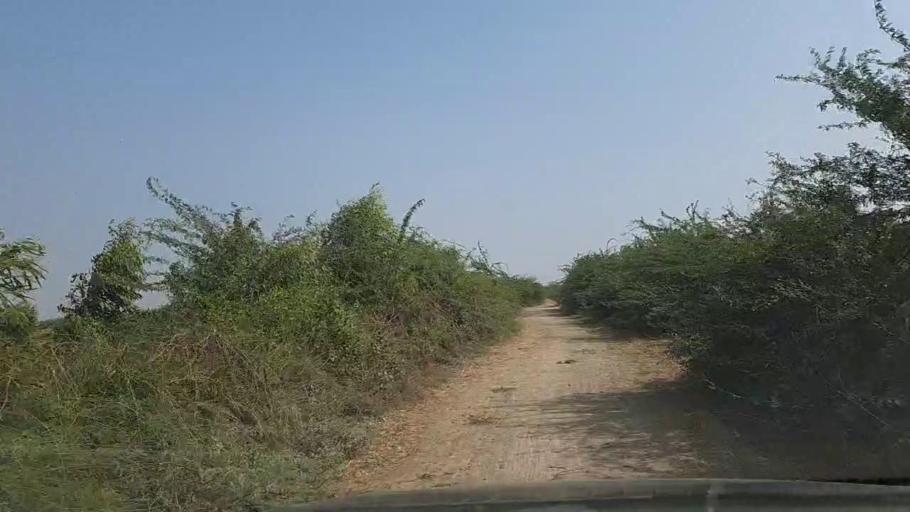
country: PK
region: Sindh
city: Gharo
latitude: 24.7390
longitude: 67.6842
